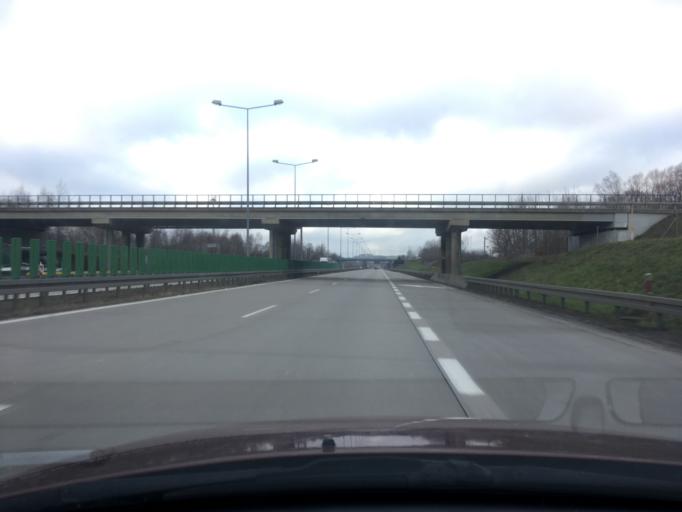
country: PL
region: Lower Silesian Voivodeship
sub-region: Powiat zgorzelecki
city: Lagow
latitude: 51.1753
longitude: 15.0223
